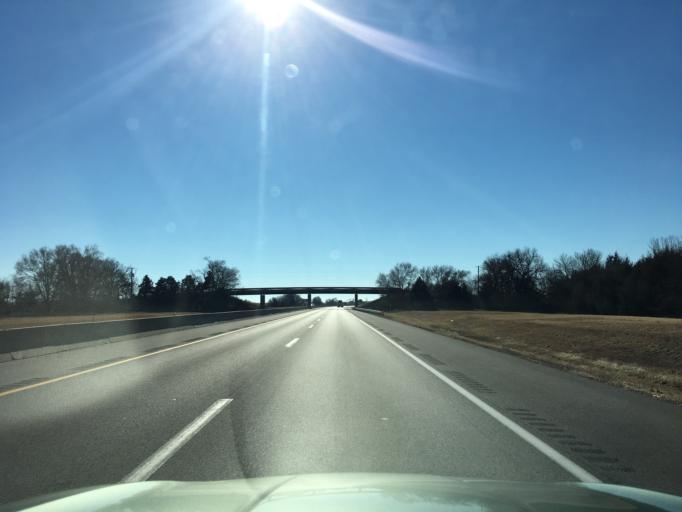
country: US
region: Kansas
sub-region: Sumner County
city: Wellington
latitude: 37.3209
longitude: -97.3397
